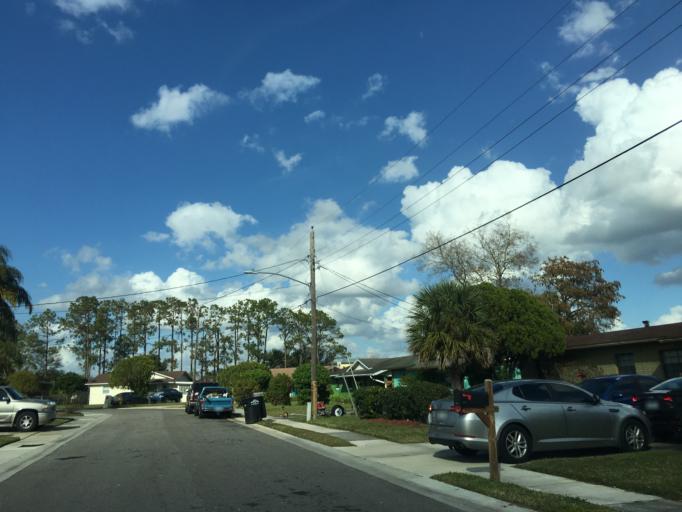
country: US
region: Florida
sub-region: Orange County
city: Eatonville
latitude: 28.6141
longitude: -81.3926
